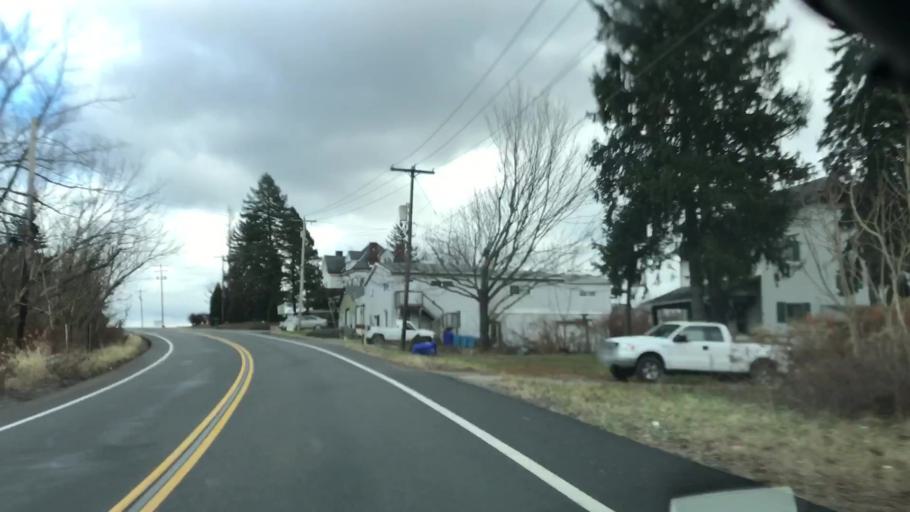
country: US
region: Pennsylvania
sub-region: Allegheny County
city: Enlow
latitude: 40.4405
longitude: -80.2314
